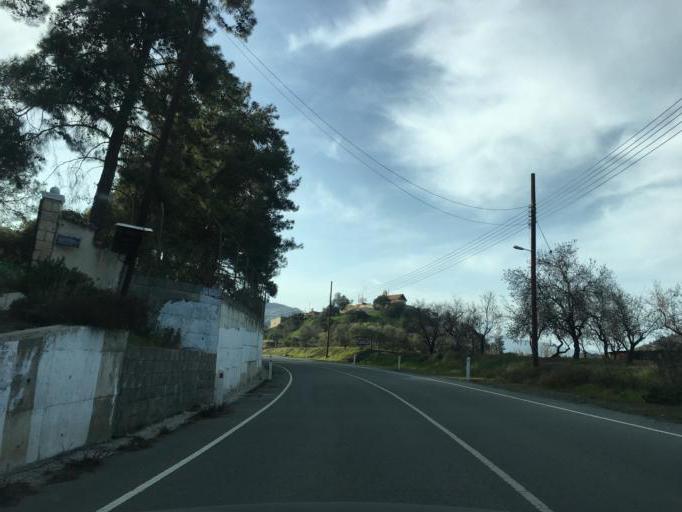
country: CY
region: Limassol
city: Pelendri
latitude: 34.8303
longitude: 32.9615
